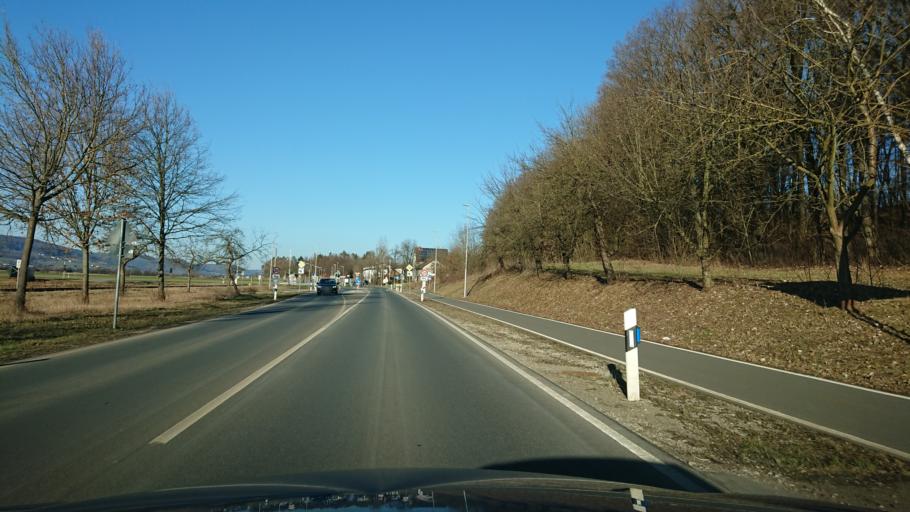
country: DE
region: Bavaria
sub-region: Upper Franconia
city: Wiesenthau
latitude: 49.7121
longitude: 11.1256
